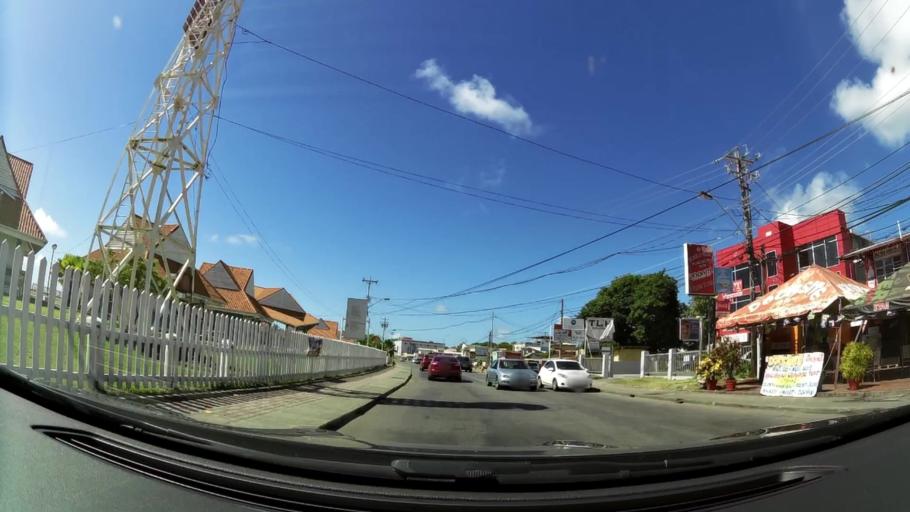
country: TT
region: Tobago
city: Scarborough
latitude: 11.1823
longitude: -60.7398
